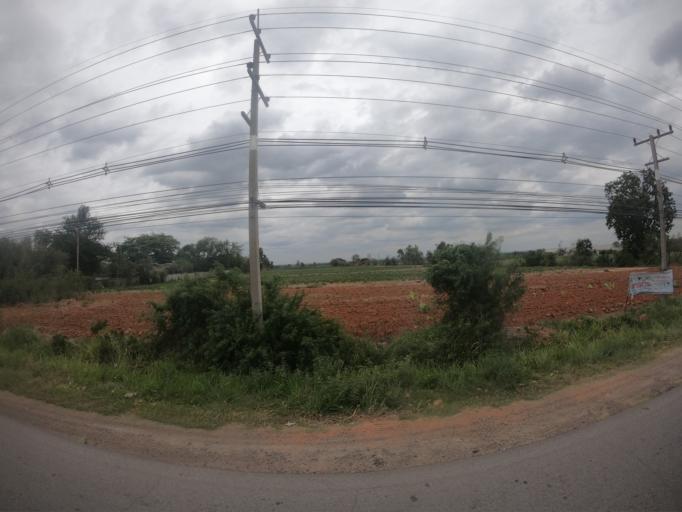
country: TH
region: Nakhon Ratchasima
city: Chok Chai
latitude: 14.7778
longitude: 102.1626
